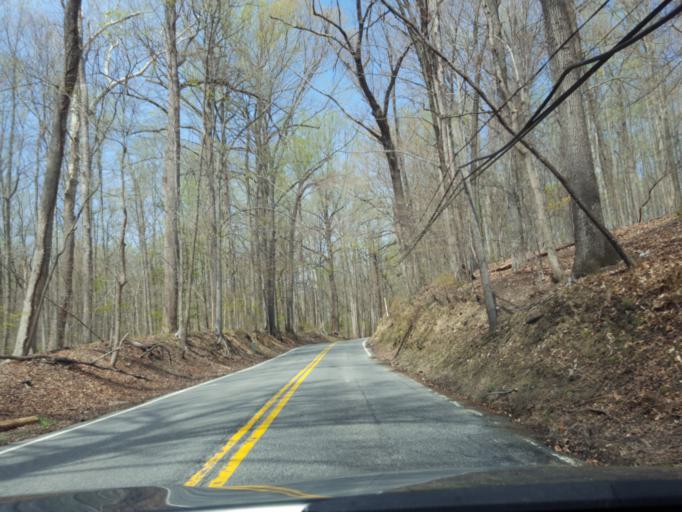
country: US
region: Maryland
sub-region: Prince George's County
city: Upper Marlboro
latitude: 38.7888
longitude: -76.7593
